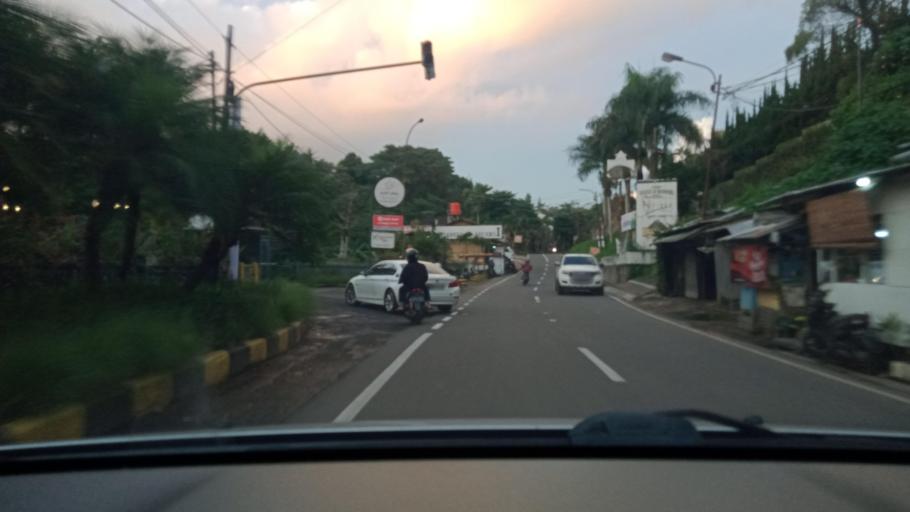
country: ID
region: West Java
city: Lembang
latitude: -6.8493
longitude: 107.5911
